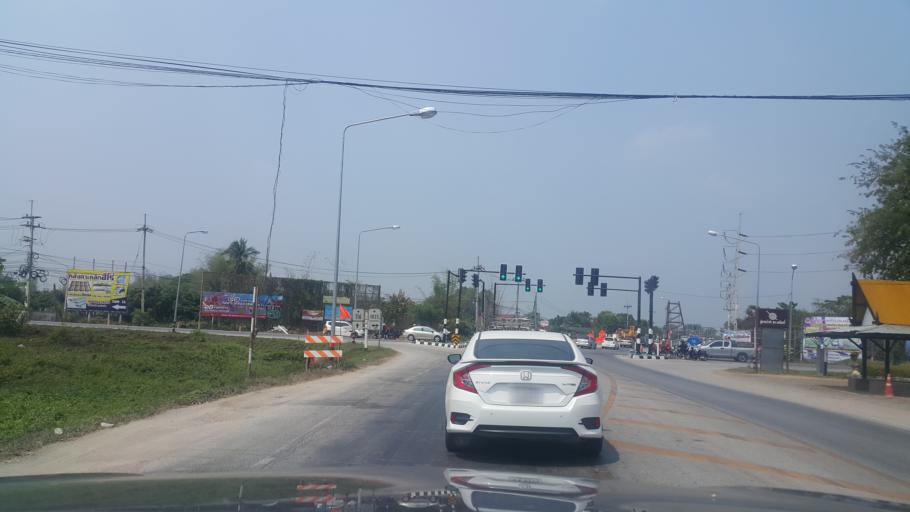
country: TH
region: Lamphun
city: Pa Sang
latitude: 18.4709
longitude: 98.9564
